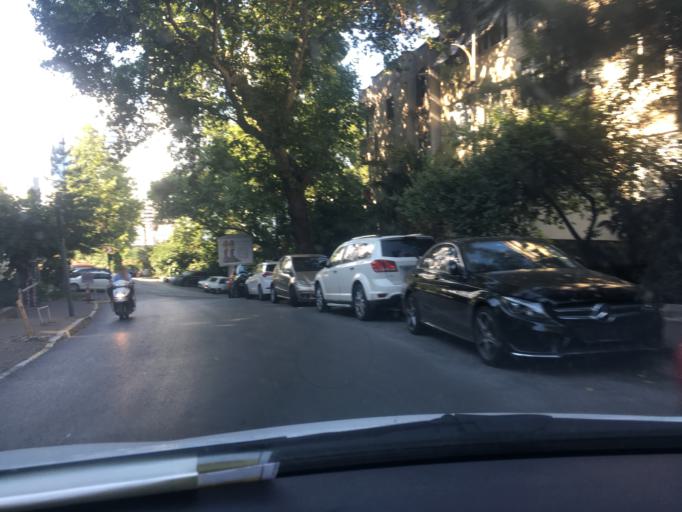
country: TR
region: Istanbul
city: Sisli
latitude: 41.0507
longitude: 29.0001
